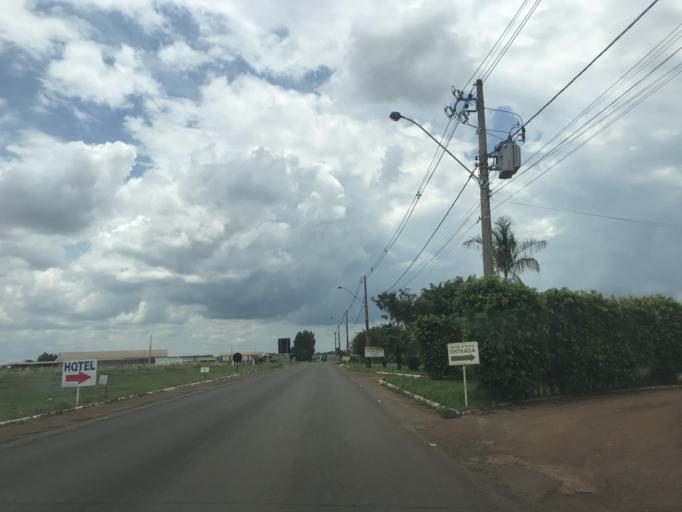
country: BR
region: Goias
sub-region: Vianopolis
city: Vianopolis
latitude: -16.7637
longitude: -48.5216
